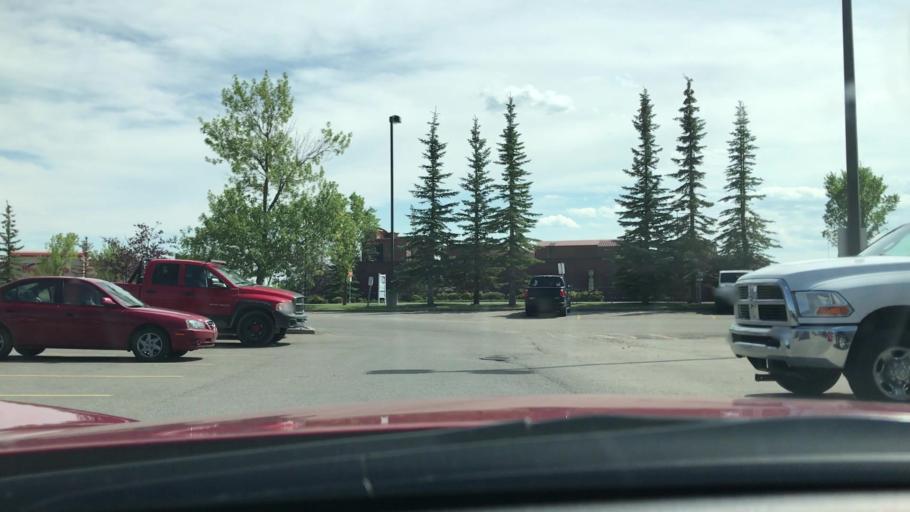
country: CA
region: Alberta
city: Calgary
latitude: 51.0184
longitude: -114.1741
